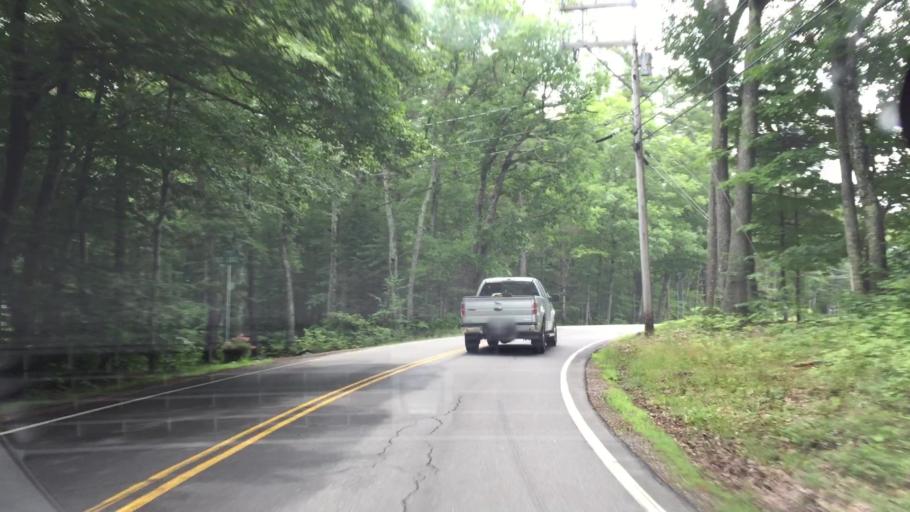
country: US
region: New Hampshire
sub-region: Grafton County
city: Holderness
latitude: 43.7555
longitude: -71.5553
